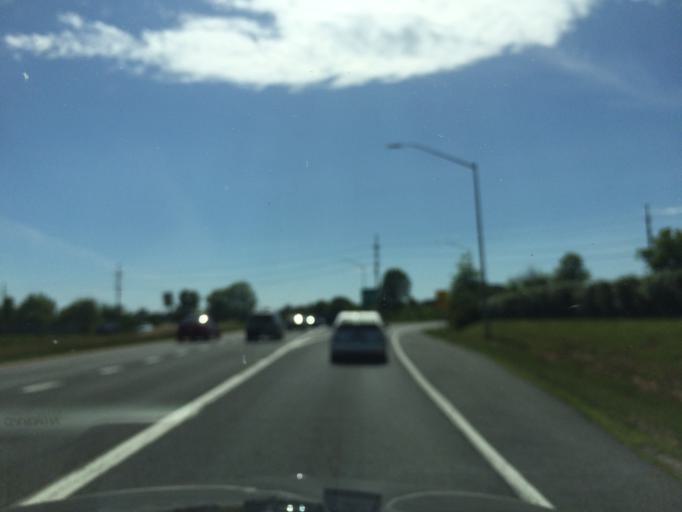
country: US
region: Maryland
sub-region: Frederick County
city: Clover Hill
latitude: 39.4444
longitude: -77.4001
